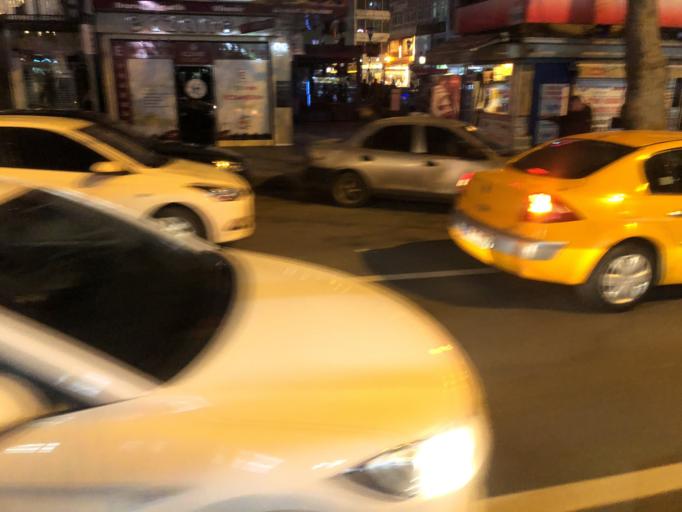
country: TR
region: Ankara
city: Ankara
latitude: 39.9238
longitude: 32.8568
